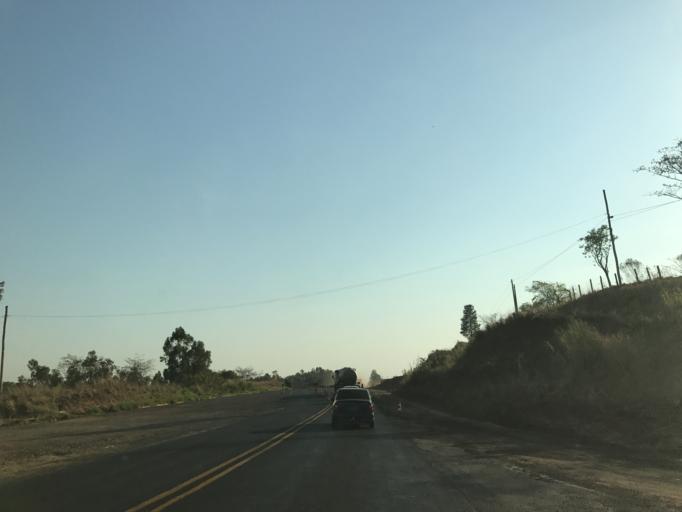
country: BR
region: Sao Paulo
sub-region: Marilia
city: Marilia
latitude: -22.1173
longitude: -49.9293
